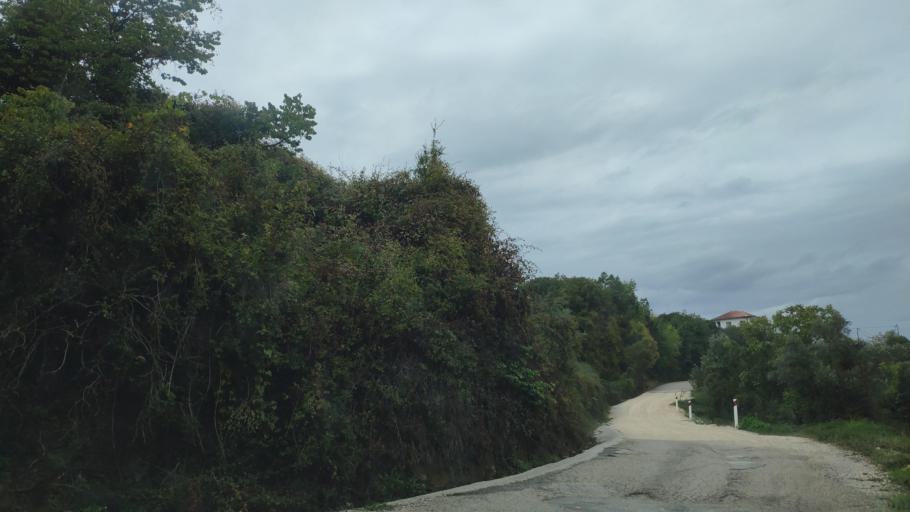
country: GR
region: Epirus
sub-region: Nomos Thesprotias
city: Paramythia
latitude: 39.4603
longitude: 20.6759
